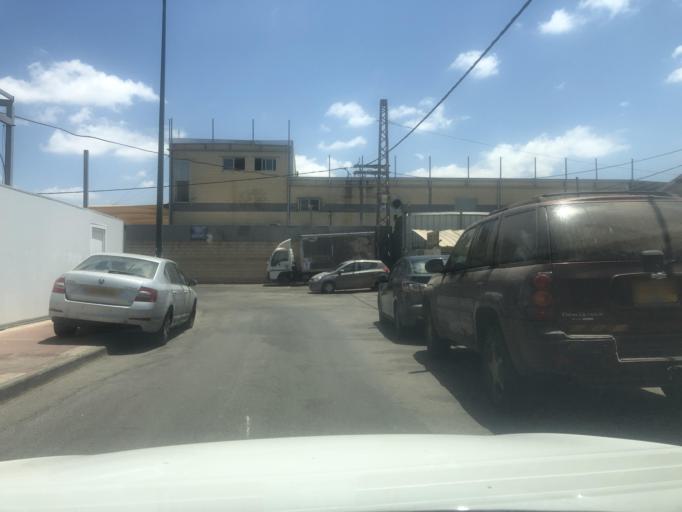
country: IL
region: Central District
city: Kfar Saba
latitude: 32.1549
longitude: 34.9207
